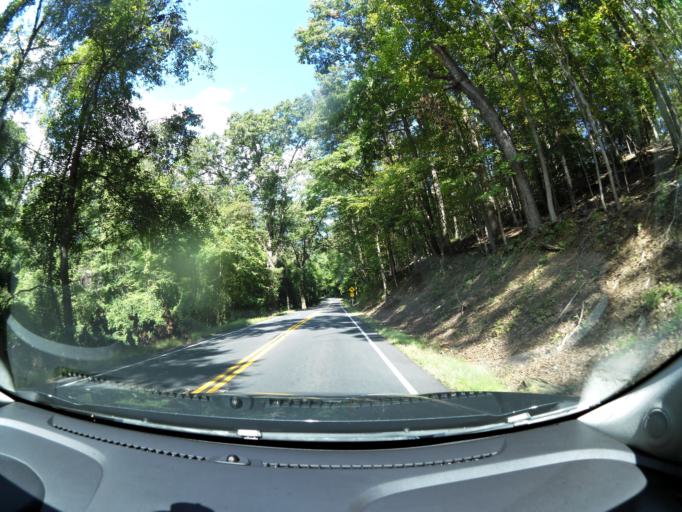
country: US
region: Virginia
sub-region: Fairfax County
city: Great Falls
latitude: 38.9795
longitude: -77.2546
